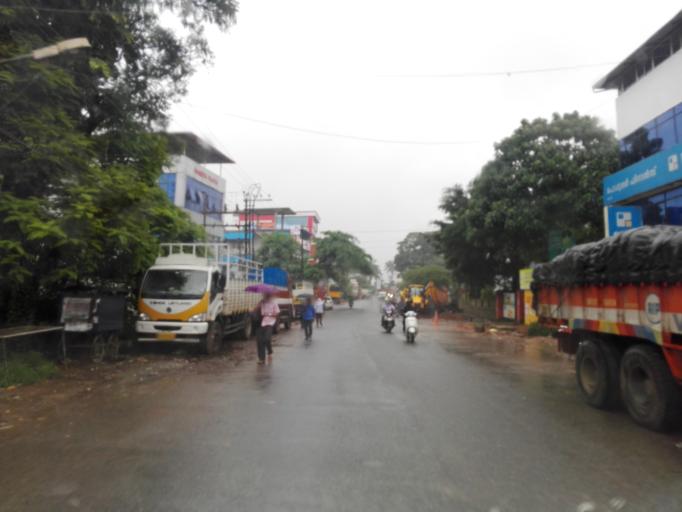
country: IN
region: Kerala
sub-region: Ernakulam
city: Elur
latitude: 10.0628
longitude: 76.3227
